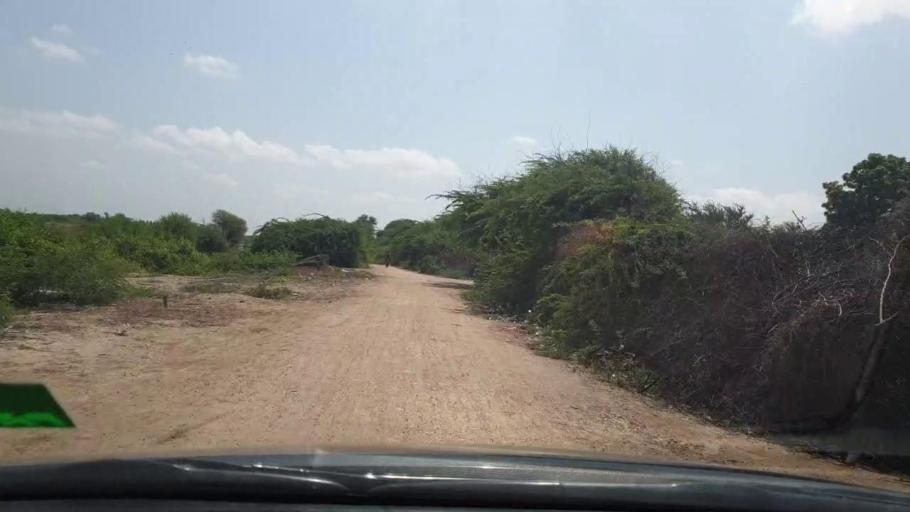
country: PK
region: Sindh
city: Tando Bago
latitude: 24.8552
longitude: 69.0883
